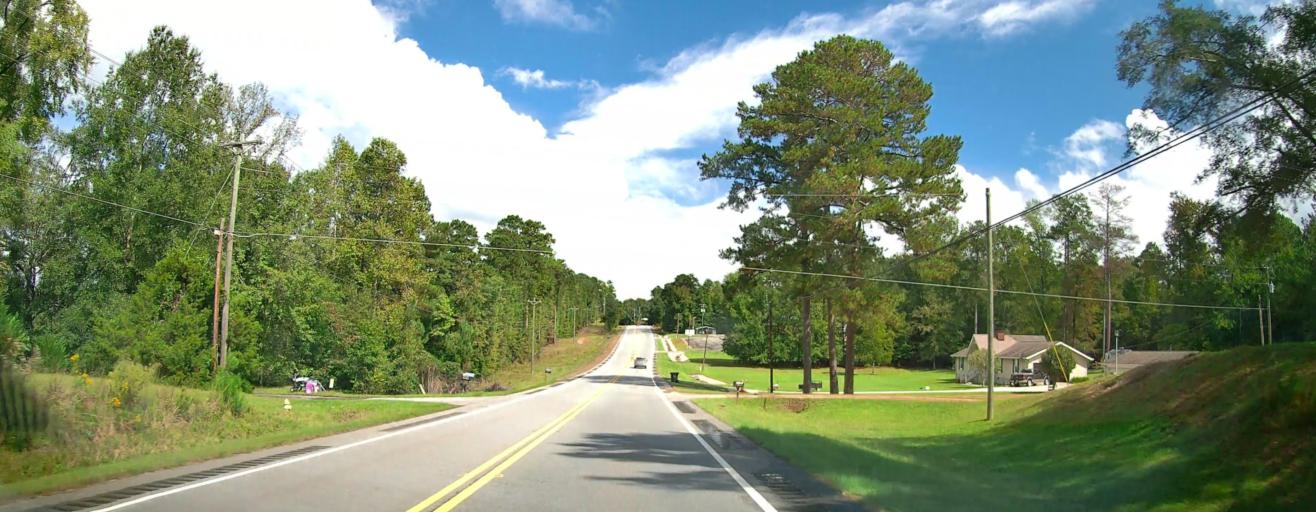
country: US
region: Georgia
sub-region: Baldwin County
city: Milledgeville
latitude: 33.0398
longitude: -83.3020
